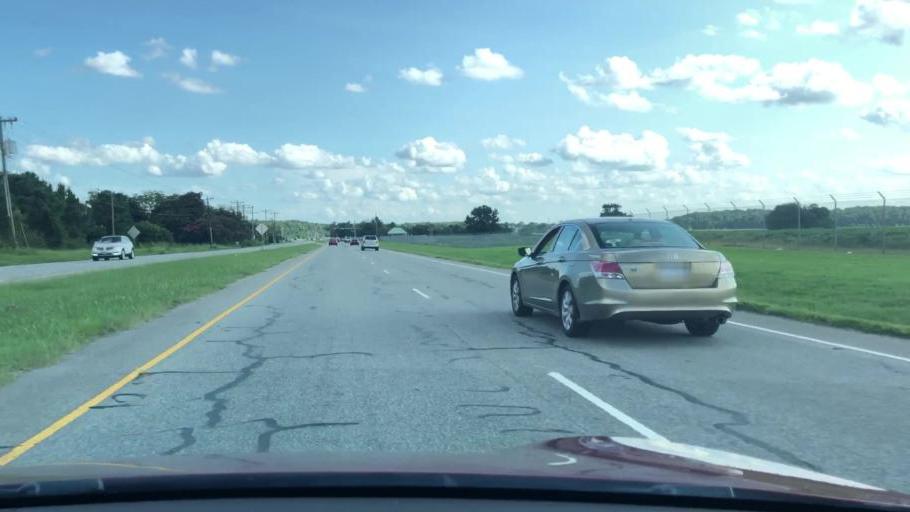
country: US
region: Virginia
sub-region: City of Virginia Beach
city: Virginia Beach
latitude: 36.8226
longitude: -76.0089
